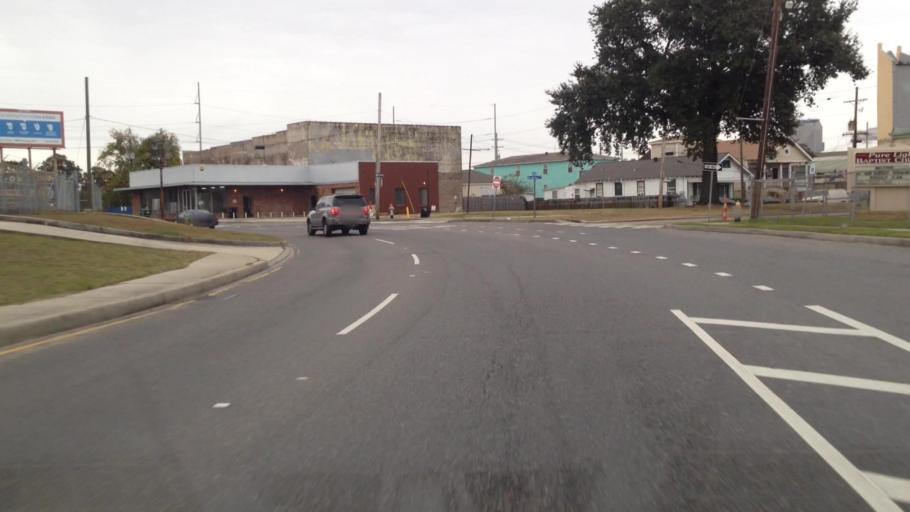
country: US
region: Louisiana
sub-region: Orleans Parish
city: New Orleans
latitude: 29.9516
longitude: -90.0986
